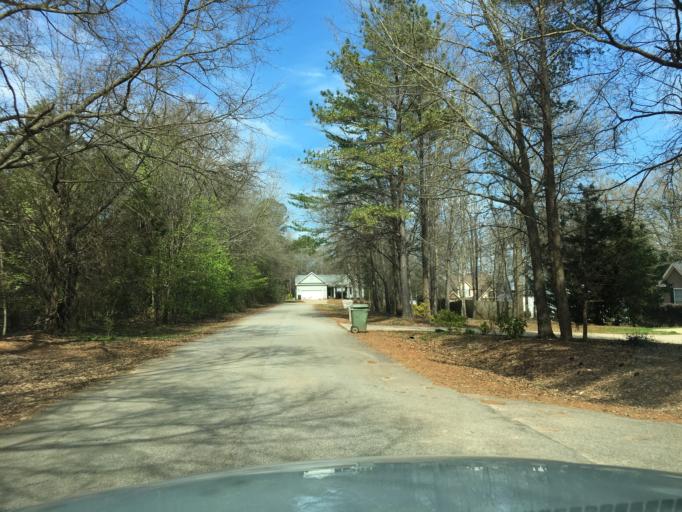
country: US
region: South Carolina
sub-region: Spartanburg County
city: Wellford
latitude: 34.9109
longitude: -82.0986
